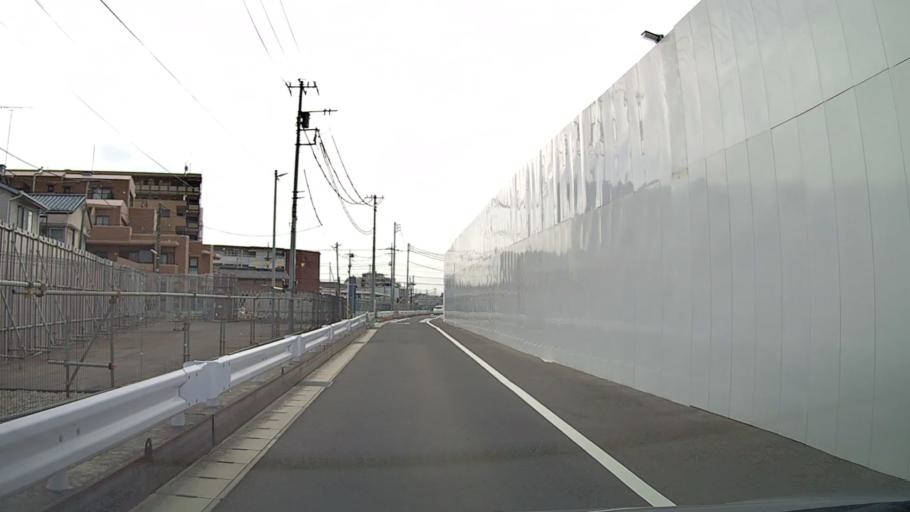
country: JP
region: Saitama
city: Wako
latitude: 35.7516
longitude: 139.5982
